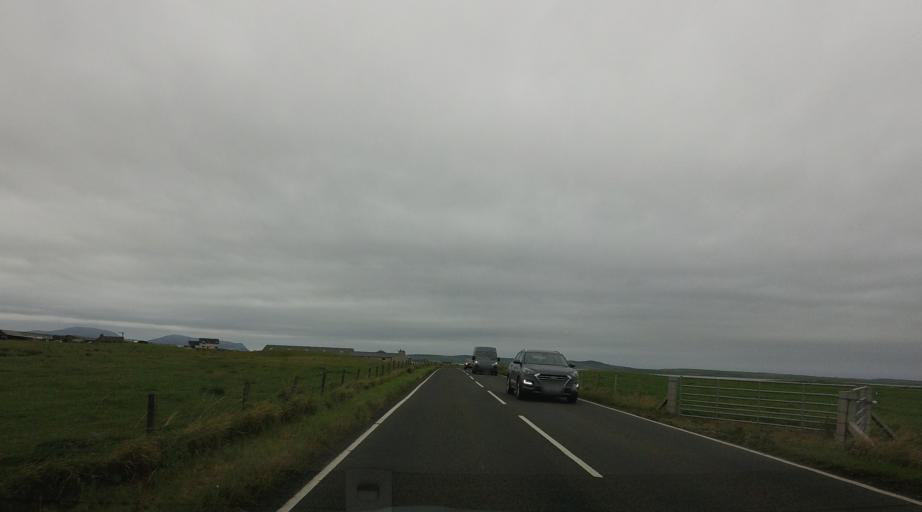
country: GB
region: Scotland
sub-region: Orkney Islands
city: Stromness
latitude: 59.0040
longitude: -3.1627
